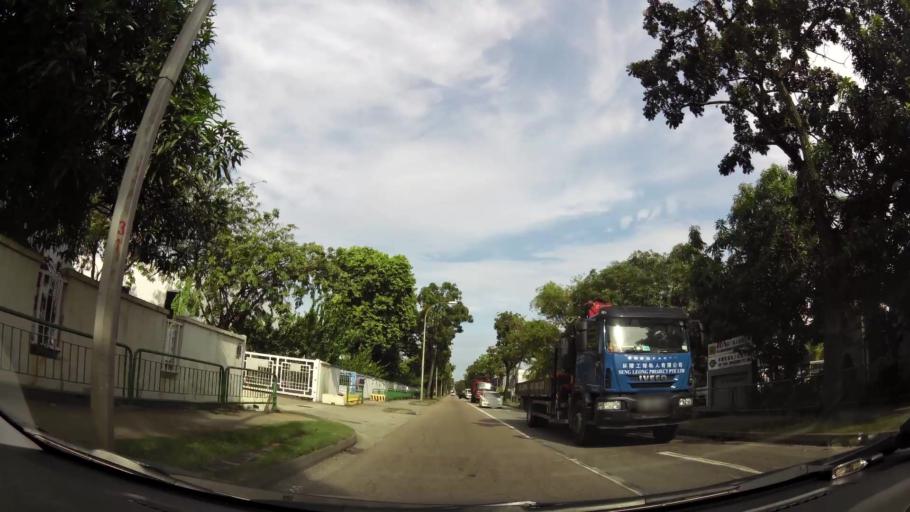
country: MY
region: Johor
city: Johor Bahru
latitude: 1.3141
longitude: 103.6548
